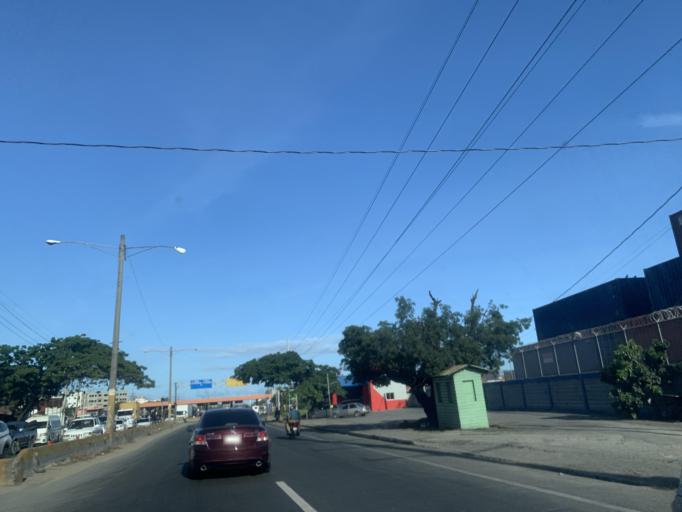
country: DO
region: San Cristobal
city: El Carril
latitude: 18.4300
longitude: -70.0030
